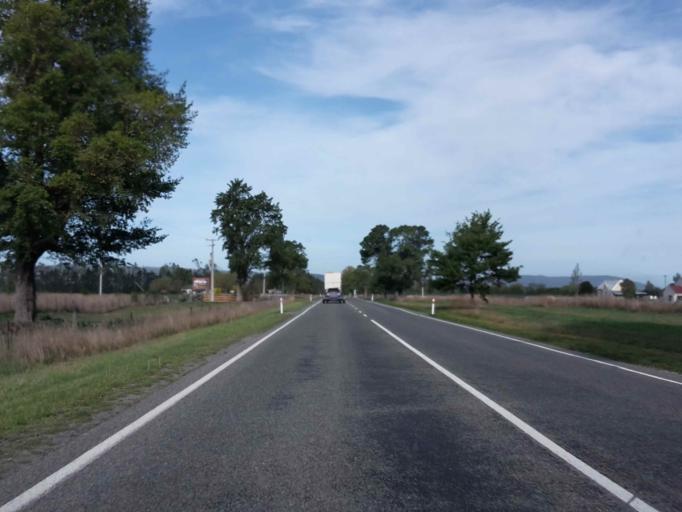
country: NZ
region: Canterbury
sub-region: Timaru District
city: Pleasant Point
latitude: -44.0732
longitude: 170.7948
